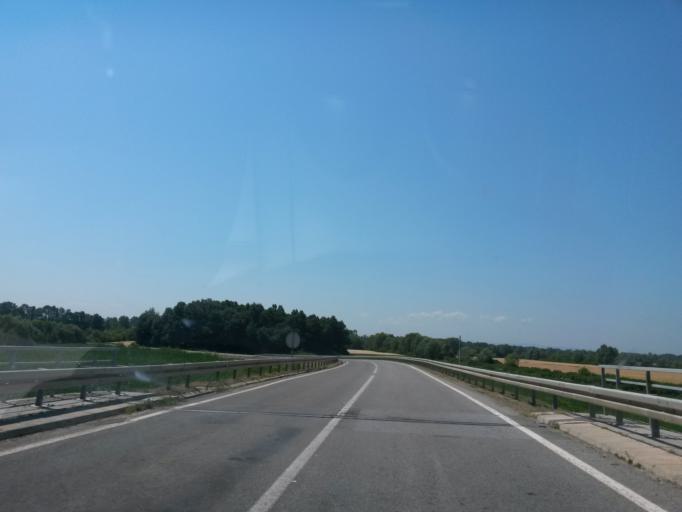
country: BA
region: Federation of Bosnia and Herzegovina
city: Donja Dubica
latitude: 45.1305
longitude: 18.4116
